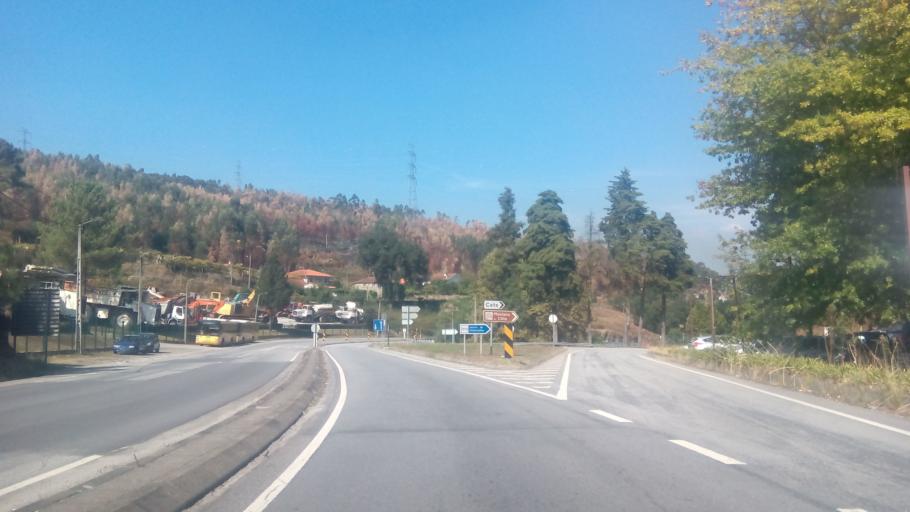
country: PT
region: Porto
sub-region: Paredes
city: Baltar
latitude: 41.1931
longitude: -8.3654
